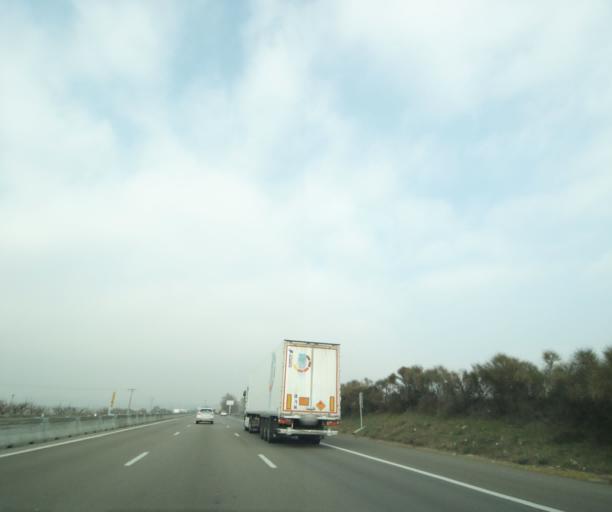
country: FR
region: Rhone-Alpes
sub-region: Departement de la Drome
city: Mercurol
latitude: 45.0539
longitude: 4.8775
